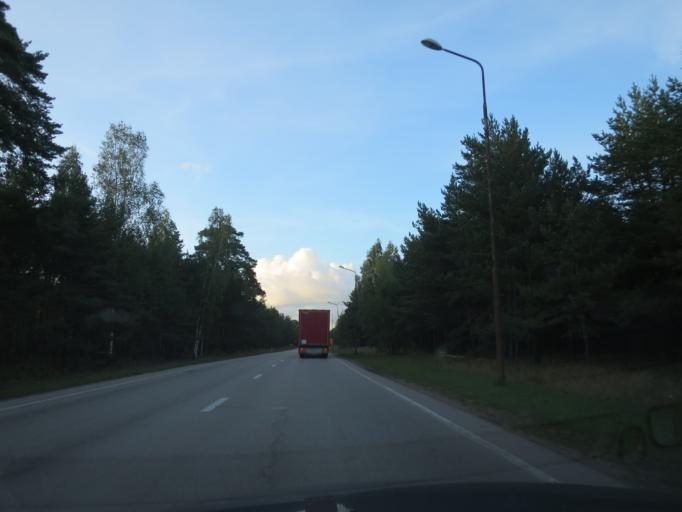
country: LV
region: Salacgrivas
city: Salacgriva
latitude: 57.7644
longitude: 24.3563
